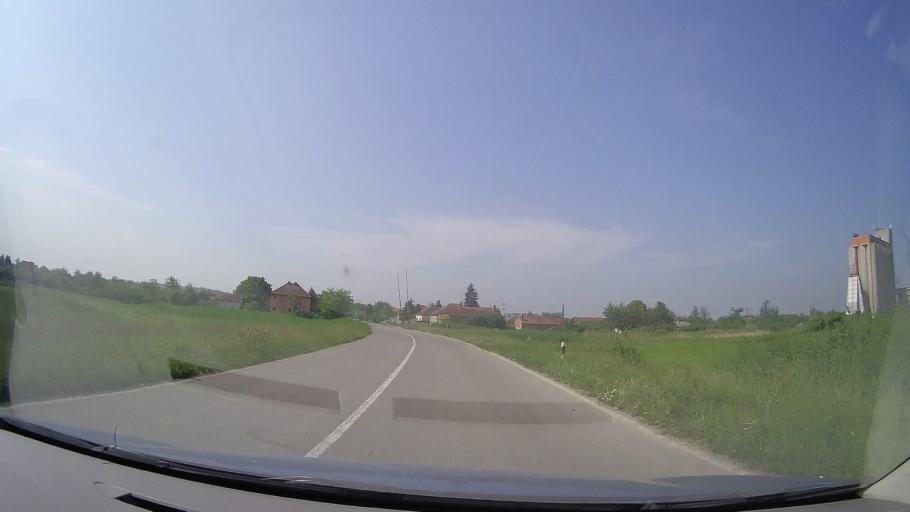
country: RS
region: Autonomna Pokrajina Vojvodina
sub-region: Srednjebanatski Okrug
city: Secanj
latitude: 45.3746
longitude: 20.7782
